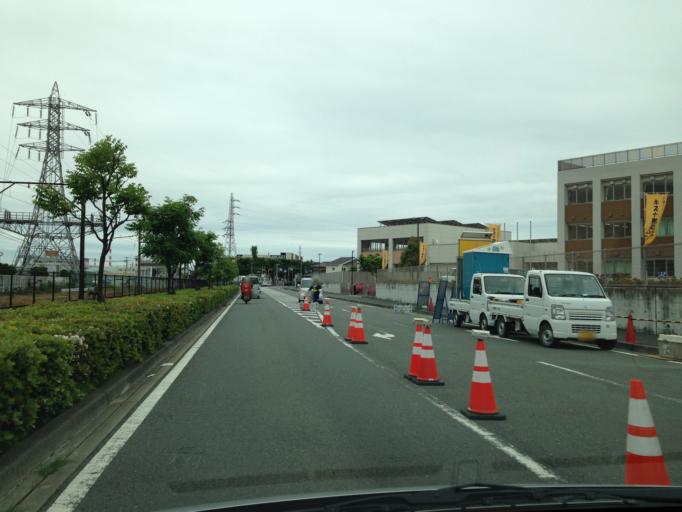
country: JP
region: Shizuoka
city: Fuji
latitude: 35.1567
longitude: 138.6909
